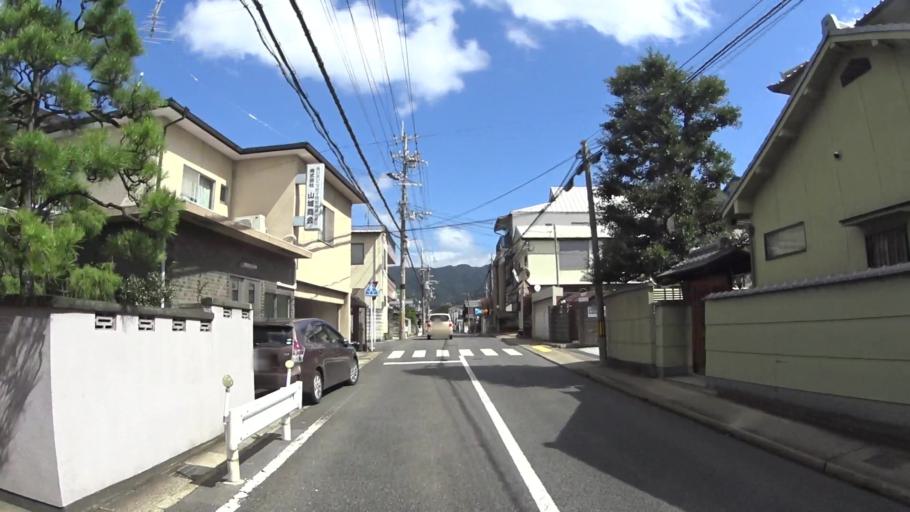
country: JP
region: Kyoto
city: Uji
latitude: 34.9349
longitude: 135.8016
